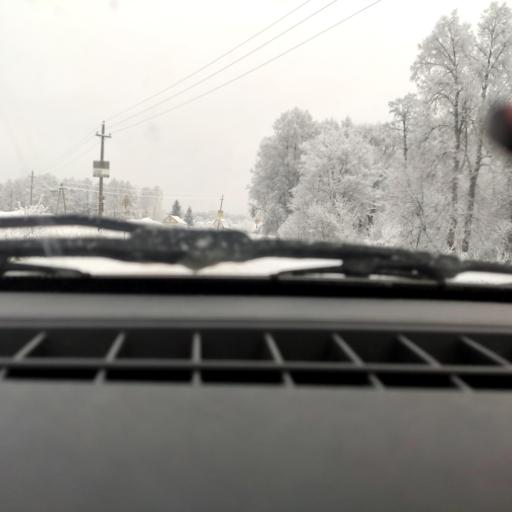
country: RU
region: Bashkortostan
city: Ufa
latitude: 54.7059
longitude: 56.1289
